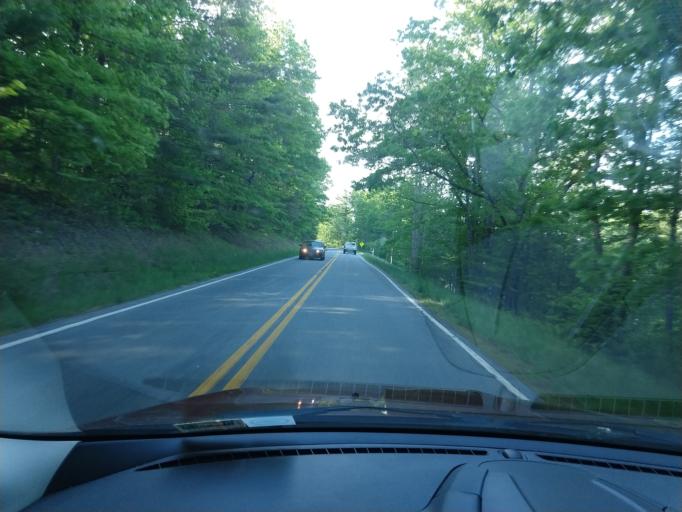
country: US
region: Virginia
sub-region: City of Galax
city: Galax
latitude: 36.7394
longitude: -80.9786
